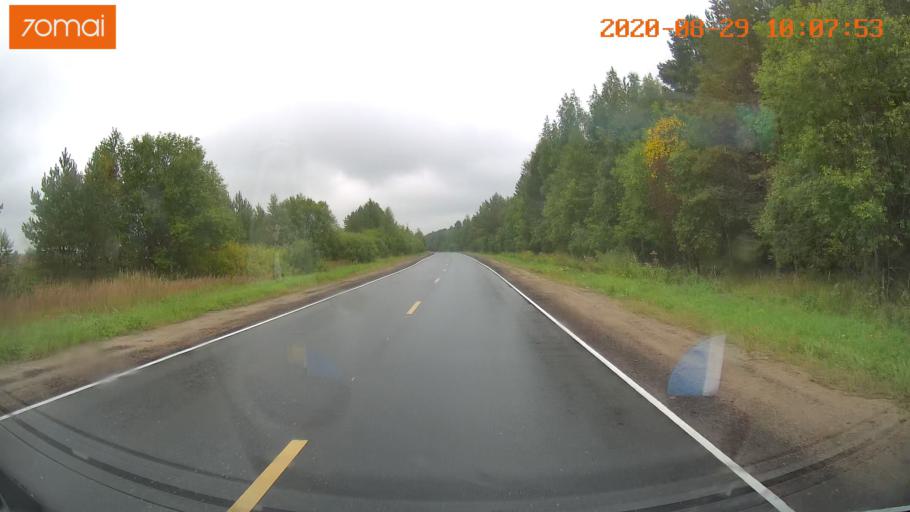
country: RU
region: Ivanovo
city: Kuznechikha
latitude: 57.3780
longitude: 42.5765
